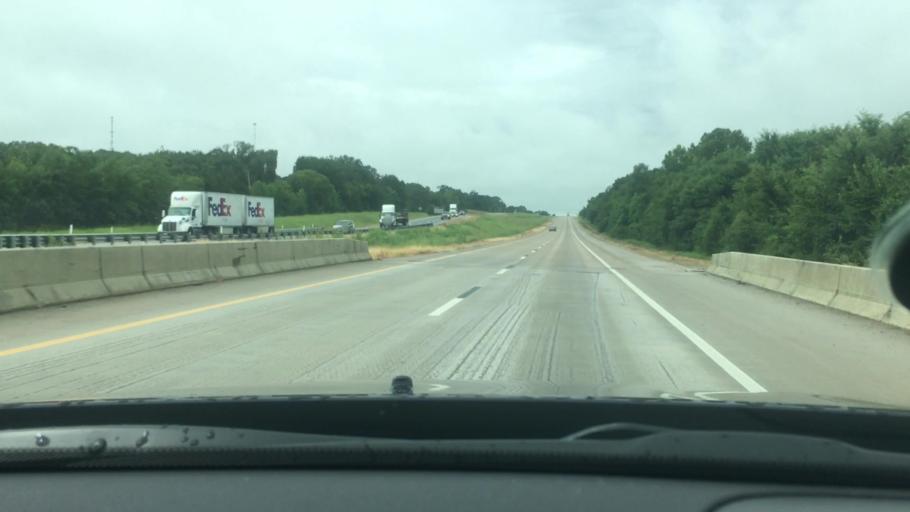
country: US
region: Oklahoma
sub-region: Atoka County
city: Atoka
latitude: 34.2414
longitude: -96.2194
